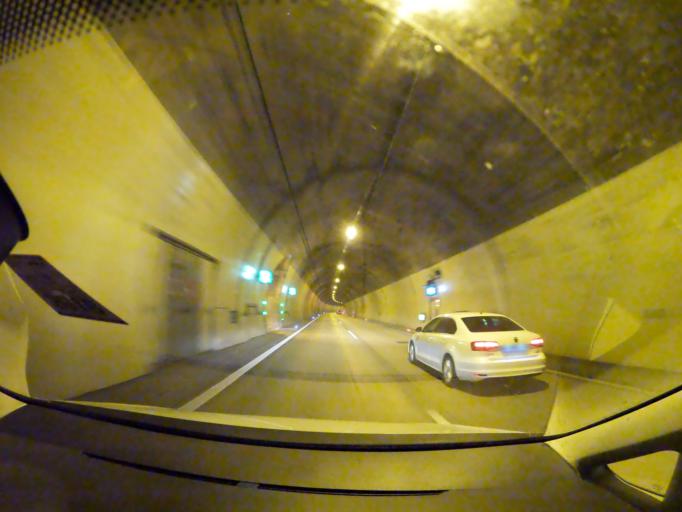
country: AT
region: Styria
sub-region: Politischer Bezirk Voitsberg
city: Modriach
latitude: 46.9629
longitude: 15.0839
